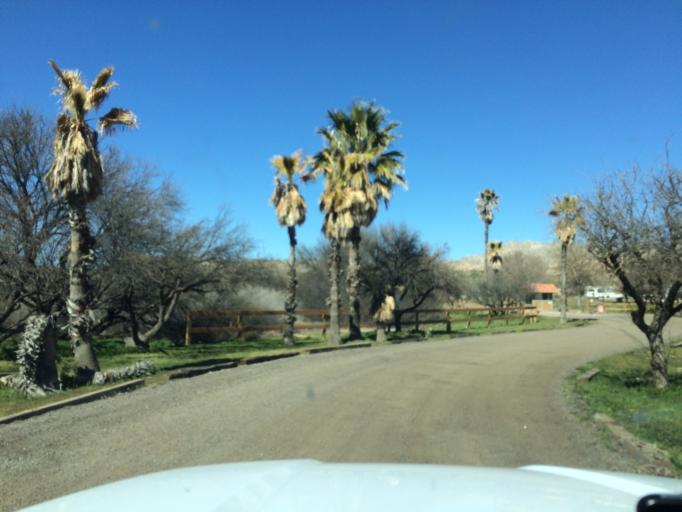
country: MX
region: Baja California
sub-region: Tecate
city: Cereso del Hongo
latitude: 32.6518
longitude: -116.1870
